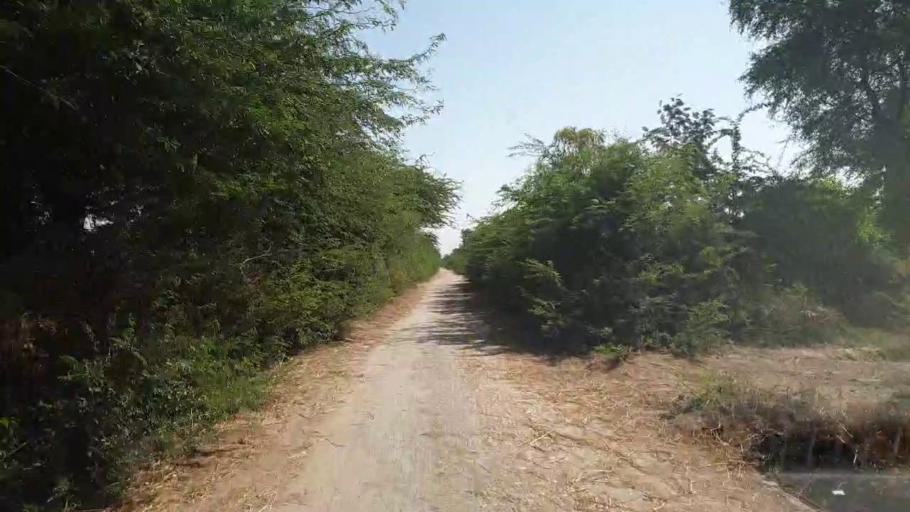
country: PK
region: Sindh
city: Tando Bago
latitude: 24.6560
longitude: 68.9805
